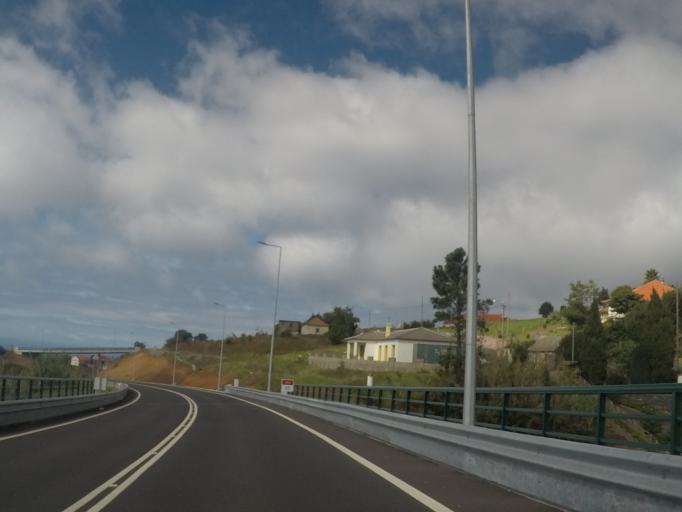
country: PT
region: Madeira
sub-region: Calheta
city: Faja da Ovelha
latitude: 32.7990
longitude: -17.2338
